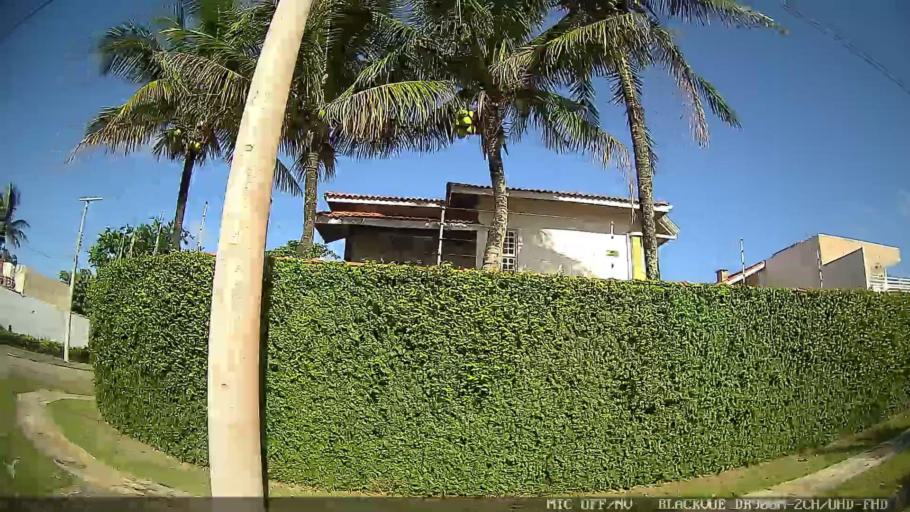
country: BR
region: Sao Paulo
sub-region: Peruibe
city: Peruibe
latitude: -24.2879
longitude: -46.9545
